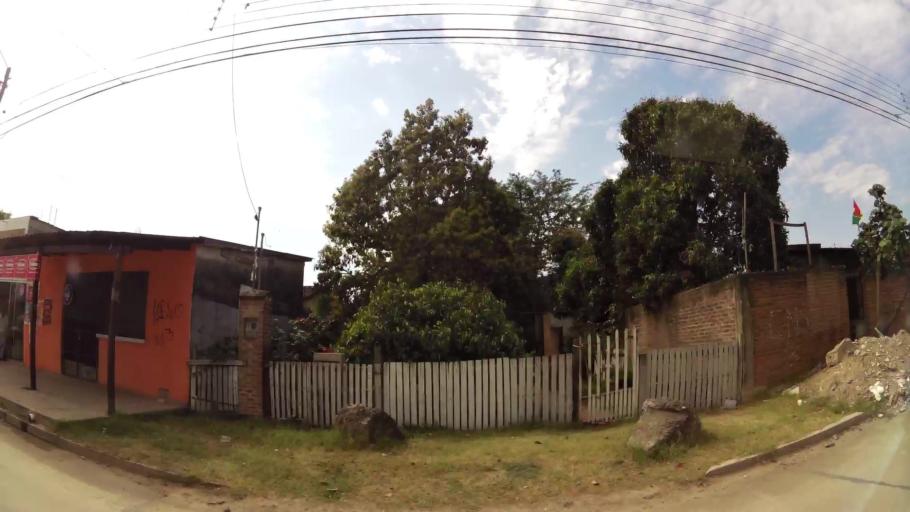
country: BO
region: Santa Cruz
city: Santa Cruz de la Sierra
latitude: -17.7306
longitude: -63.1805
